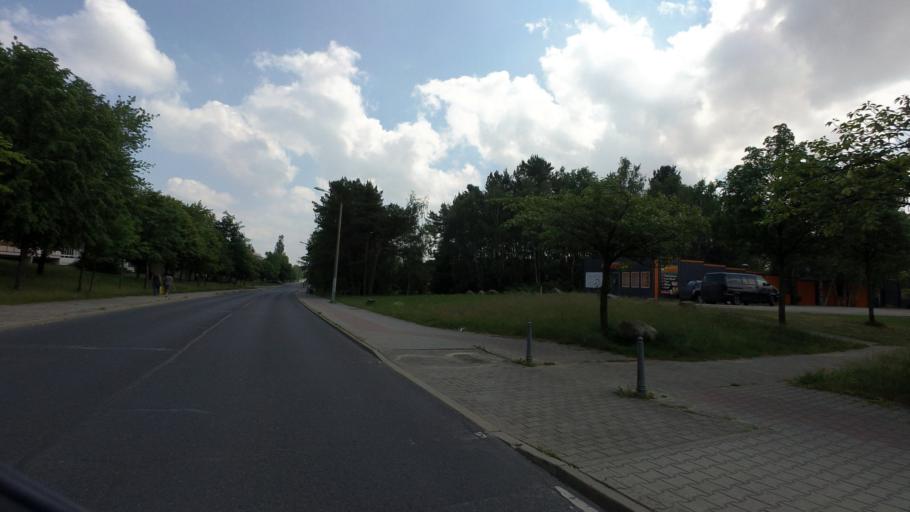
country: DE
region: Saxony
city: Weisswasser
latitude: 51.4986
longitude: 14.6273
